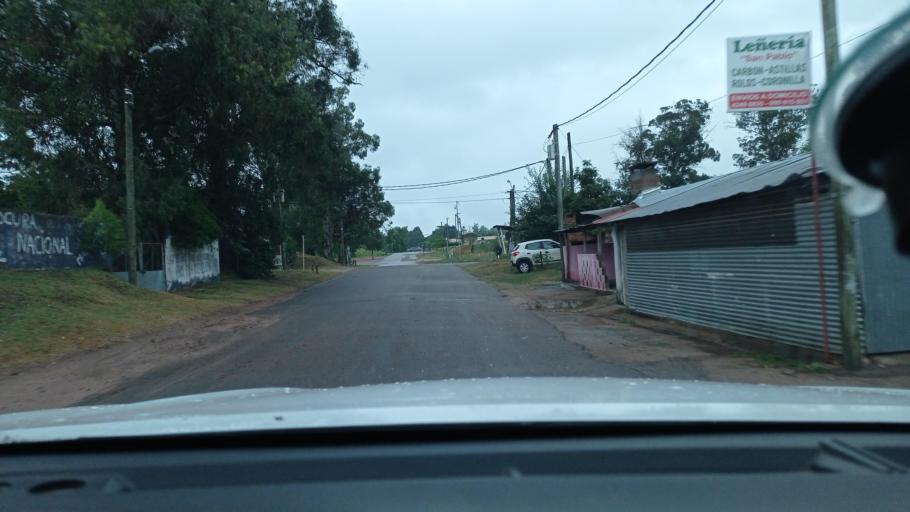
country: UY
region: Maldonado
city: Maldonado
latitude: -34.9233
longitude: -54.9120
